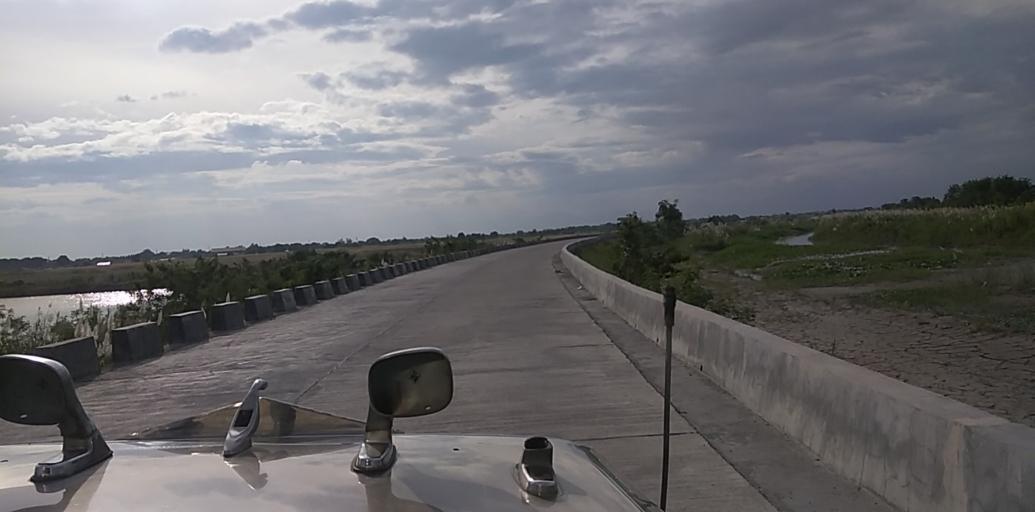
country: PH
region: Central Luzon
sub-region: Province of Pampanga
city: Minalin
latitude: 14.9668
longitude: 120.6698
